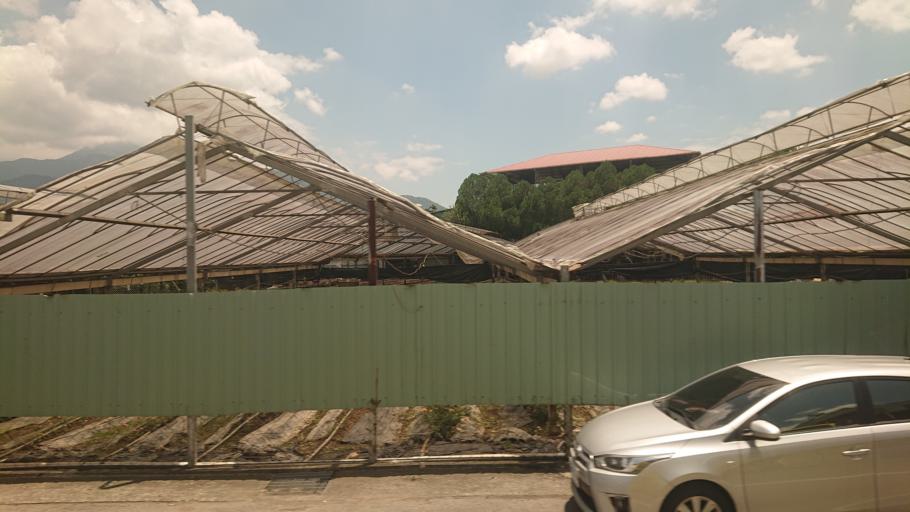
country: TW
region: Taiwan
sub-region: Nantou
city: Puli
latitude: 23.9744
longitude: 120.9626
